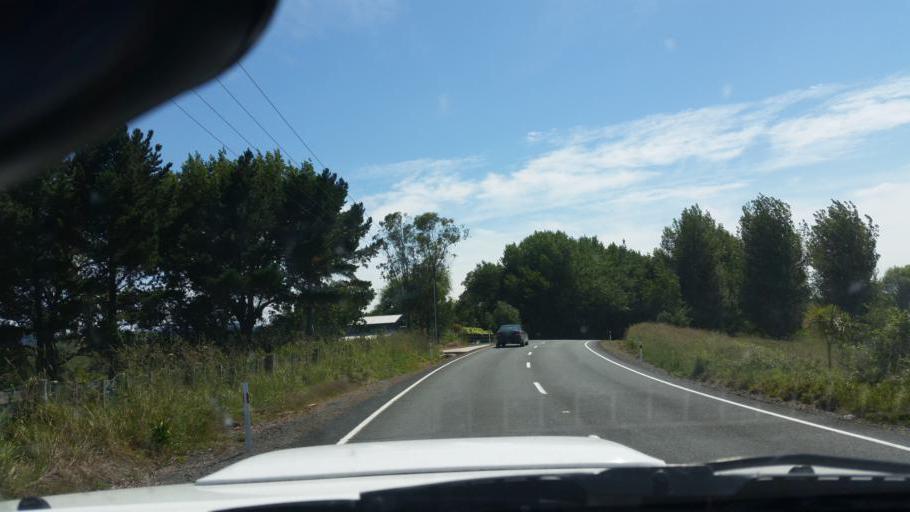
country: NZ
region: Auckland
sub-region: Auckland
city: Wellsford
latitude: -36.2193
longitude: 174.3820
